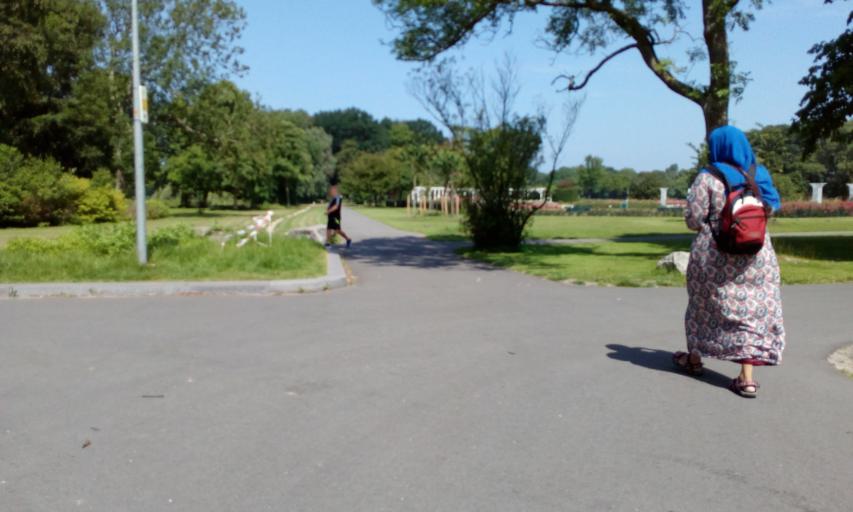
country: NL
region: South Holland
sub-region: Gemeente Den Haag
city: The Hague
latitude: 52.0559
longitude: 4.2878
